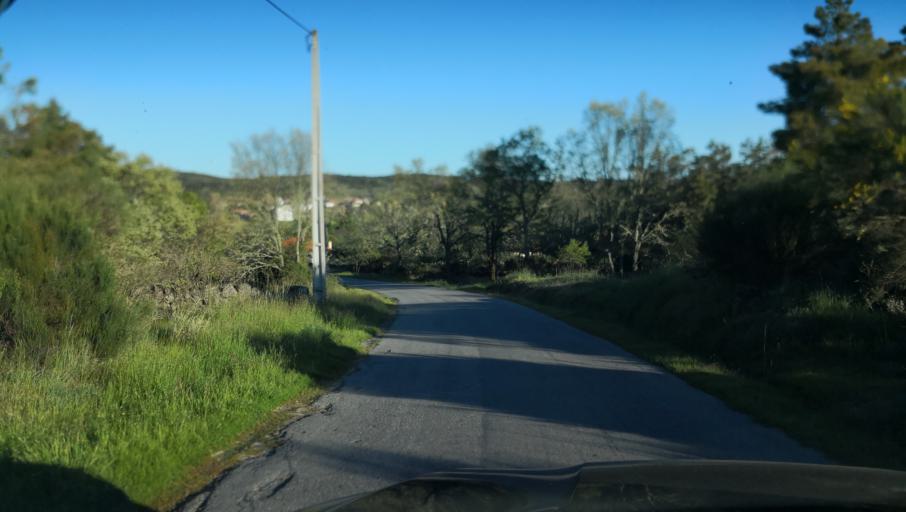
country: PT
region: Vila Real
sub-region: Vila Real
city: Vila Real
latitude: 41.3565
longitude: -7.6501
